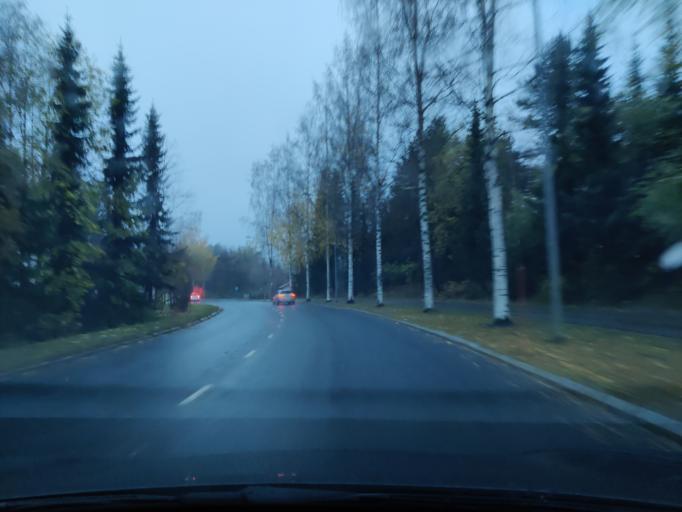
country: FI
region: Northern Savo
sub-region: Kuopio
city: Kuopio
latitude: 62.8439
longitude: 27.6580
